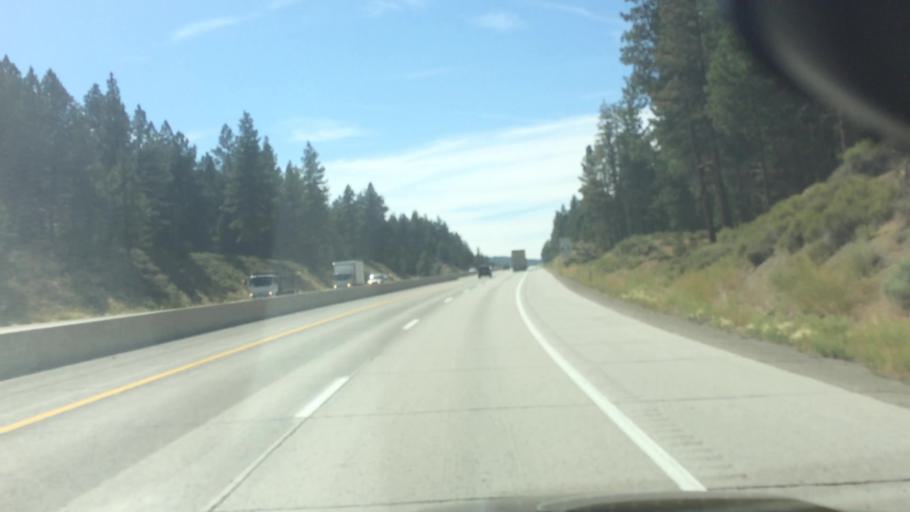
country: US
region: California
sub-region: Nevada County
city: Truckee
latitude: 39.3734
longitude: -120.0633
